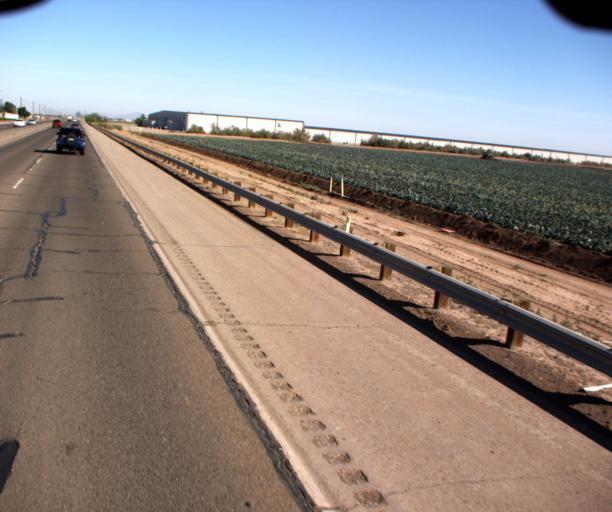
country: US
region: Arizona
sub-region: Yuma County
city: San Luis
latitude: 32.5254
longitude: -114.7866
